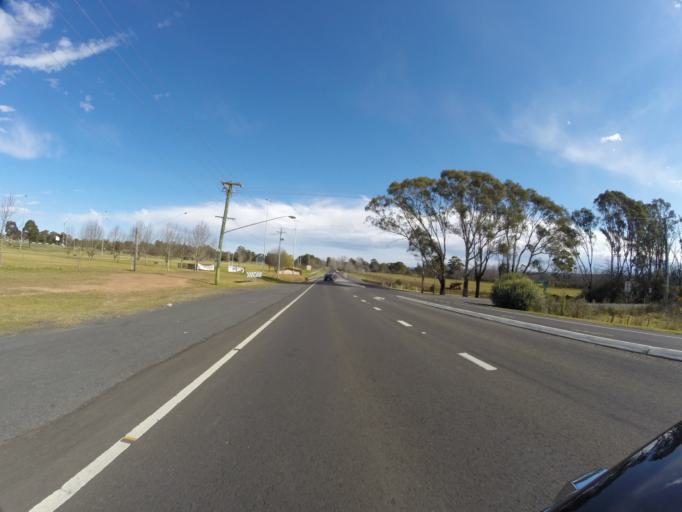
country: AU
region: New South Wales
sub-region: Camden
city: Elderslie
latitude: -34.0472
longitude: 150.7179
